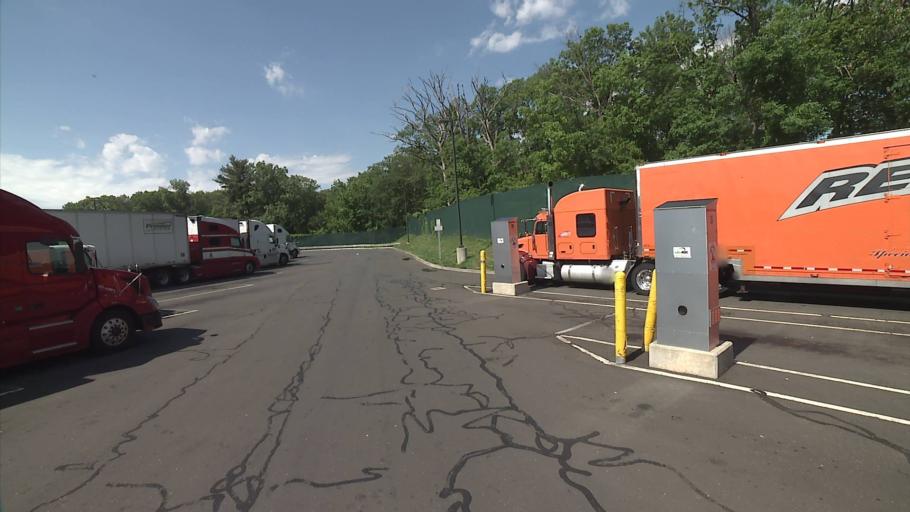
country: US
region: Connecticut
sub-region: New Haven County
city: Woodmont
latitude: 41.2473
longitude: -73.0106
